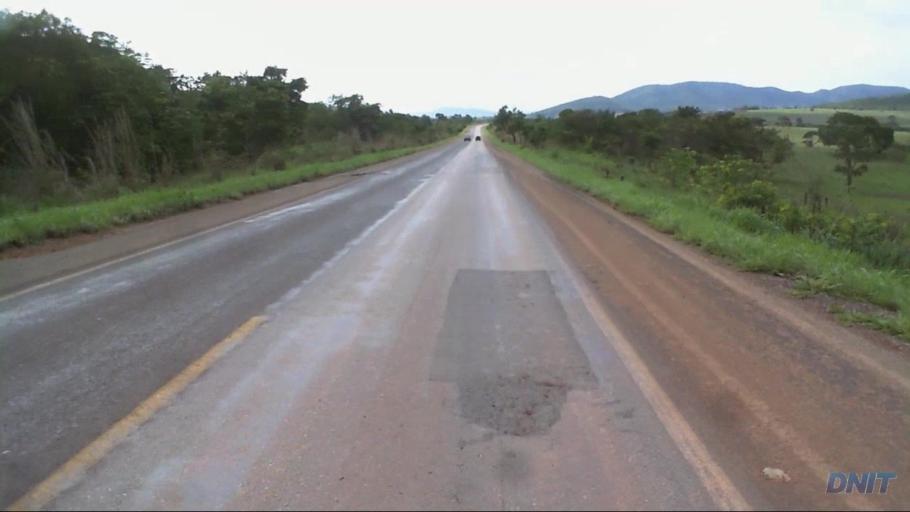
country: BR
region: Goias
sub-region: Barro Alto
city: Barro Alto
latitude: -14.9444
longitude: -48.9365
